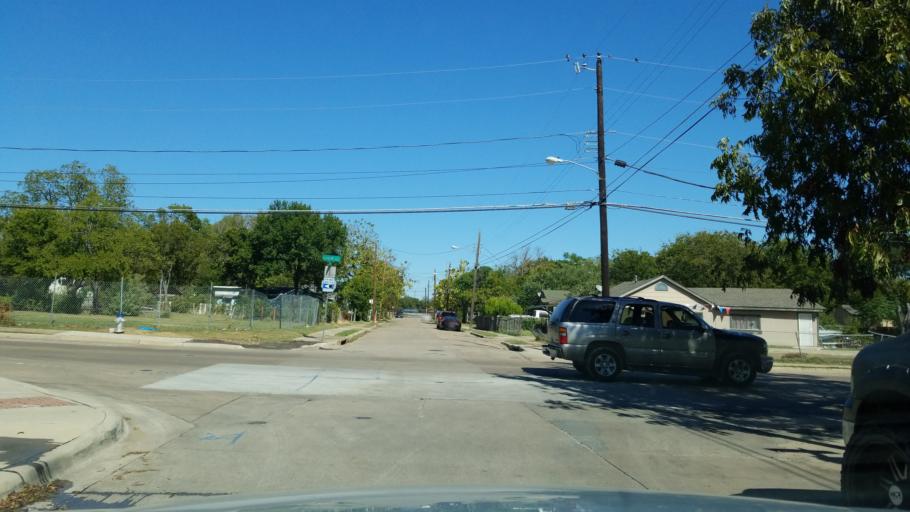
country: US
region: Texas
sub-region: Dallas County
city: Dallas
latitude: 32.7744
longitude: -96.7530
